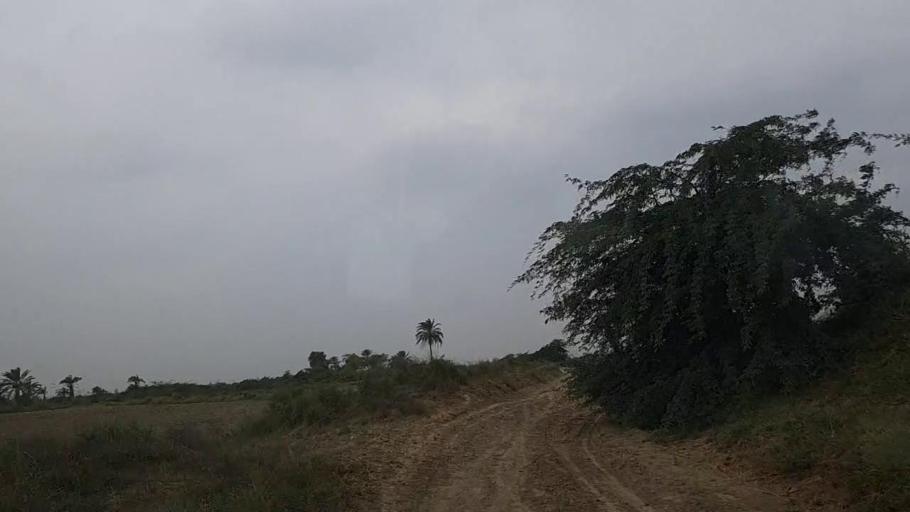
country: PK
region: Sindh
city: Mirpur Sakro
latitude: 24.5949
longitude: 67.6978
